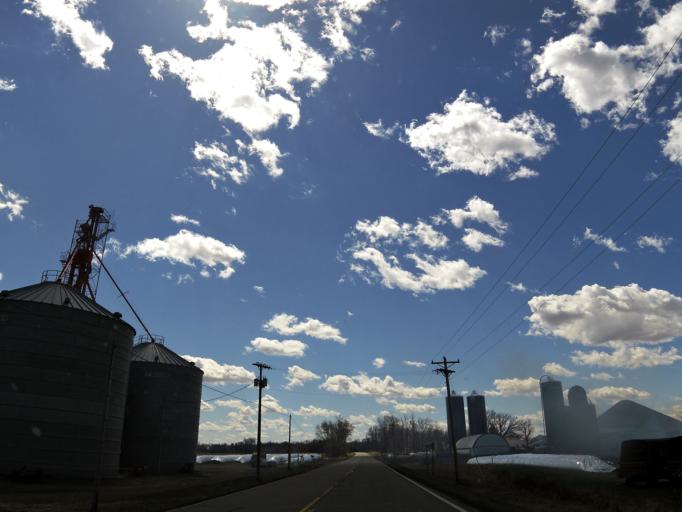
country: US
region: Minnesota
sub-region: Washington County
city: Cottage Grove
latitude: 44.7545
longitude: -92.9298
